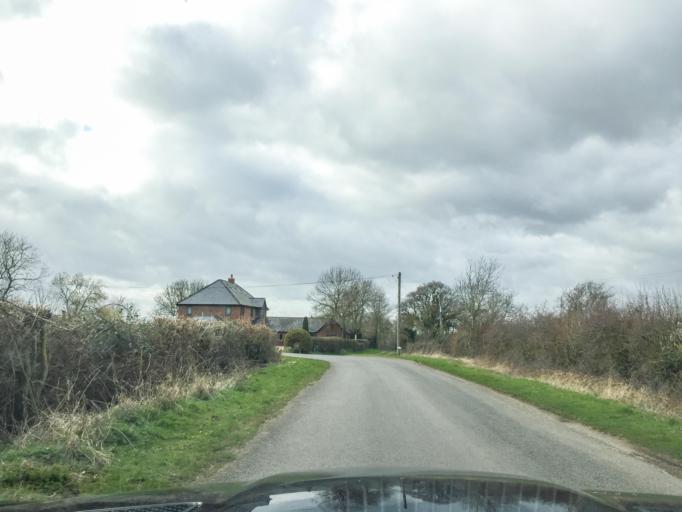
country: GB
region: England
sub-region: Warwickshire
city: Shipston on Stour
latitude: 52.0626
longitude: -1.5529
